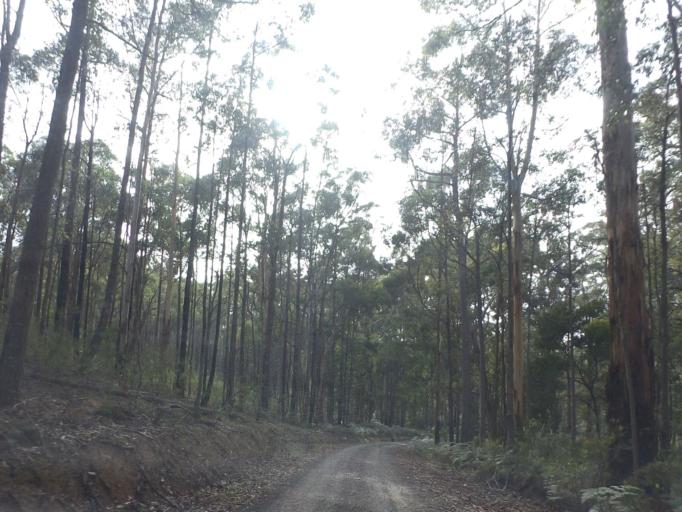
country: AU
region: Victoria
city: Brown Hill
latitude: -37.4886
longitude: 144.1724
